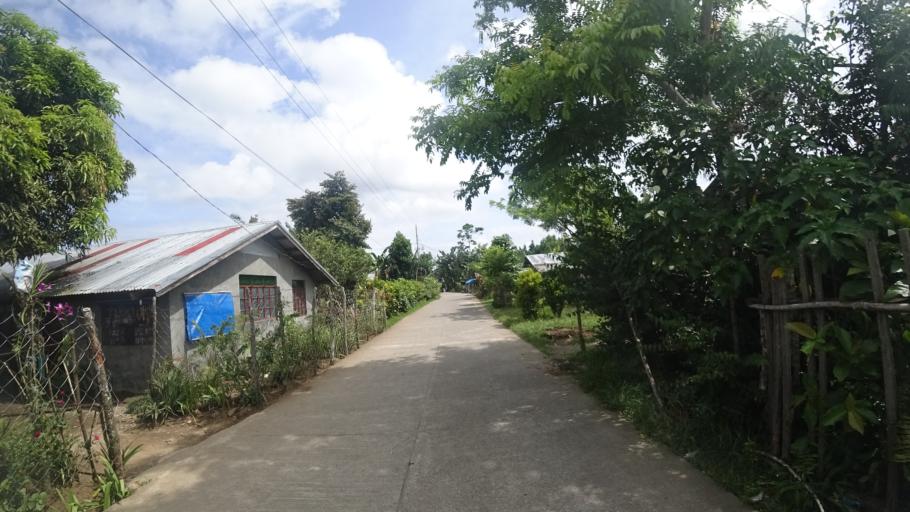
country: PH
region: Eastern Visayas
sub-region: Province of Leyte
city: Santa Fe
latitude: 11.1830
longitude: 124.8904
